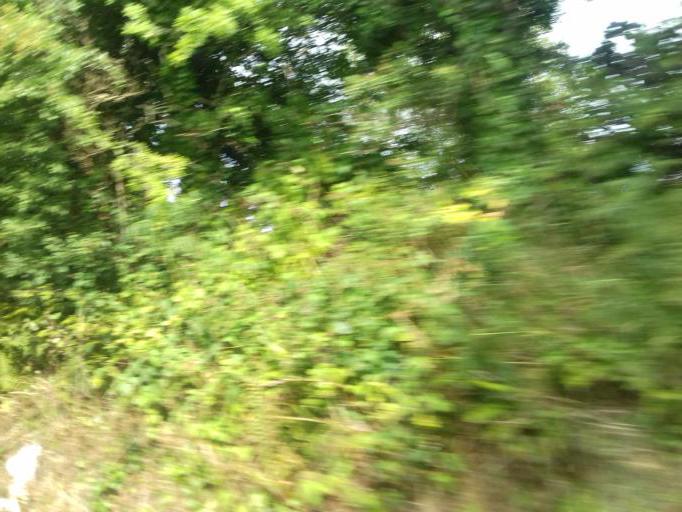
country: IE
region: Leinster
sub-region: Loch Garman
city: Loch Garman
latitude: 52.3117
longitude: -6.6498
